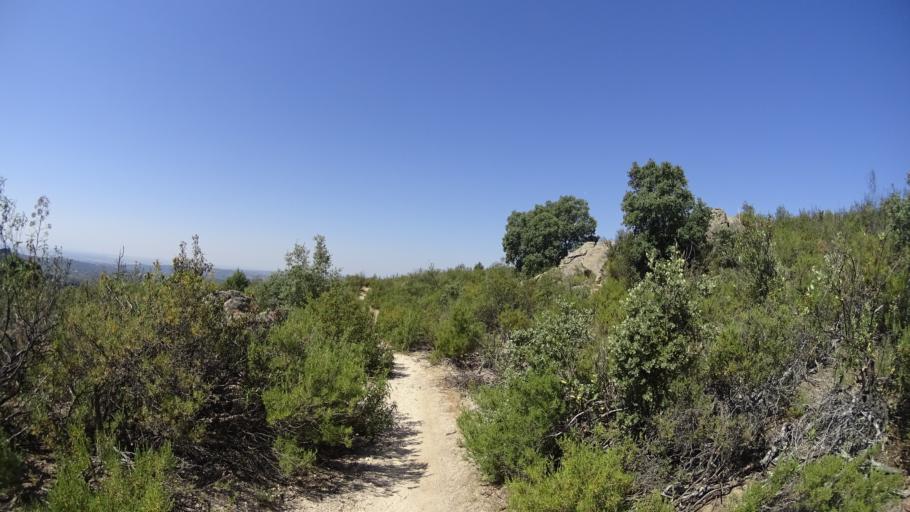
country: ES
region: Madrid
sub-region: Provincia de Madrid
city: Hoyo de Manzanares
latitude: 40.6411
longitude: -3.9403
